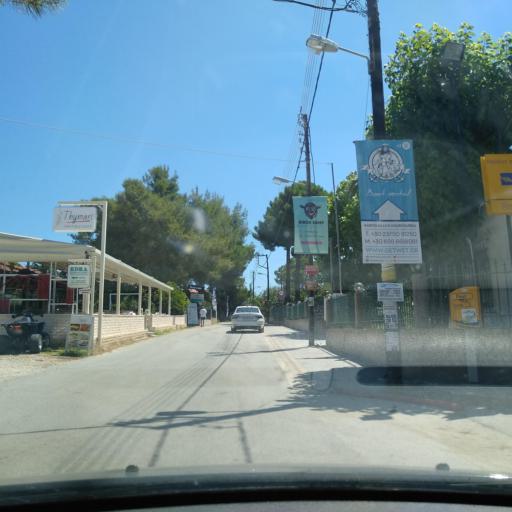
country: GR
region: Central Macedonia
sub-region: Nomos Chalkidikis
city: Neos Marmaras
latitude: 40.1880
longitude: 23.8028
